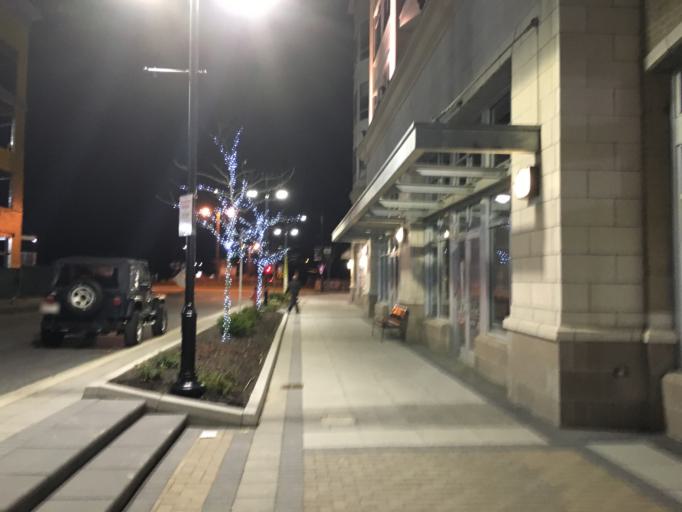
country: US
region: Maryland
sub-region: Baltimore County
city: Owings Mills
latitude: 39.4062
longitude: -76.7813
